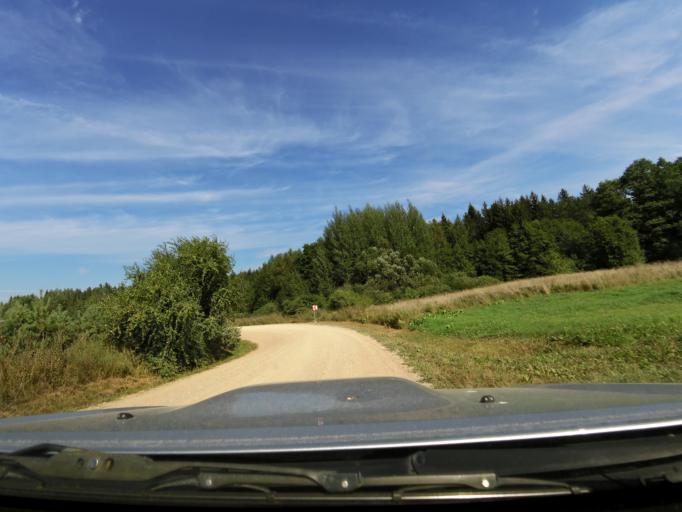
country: LT
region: Vilnius County
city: Pasilaiciai
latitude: 54.8413
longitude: 25.1712
